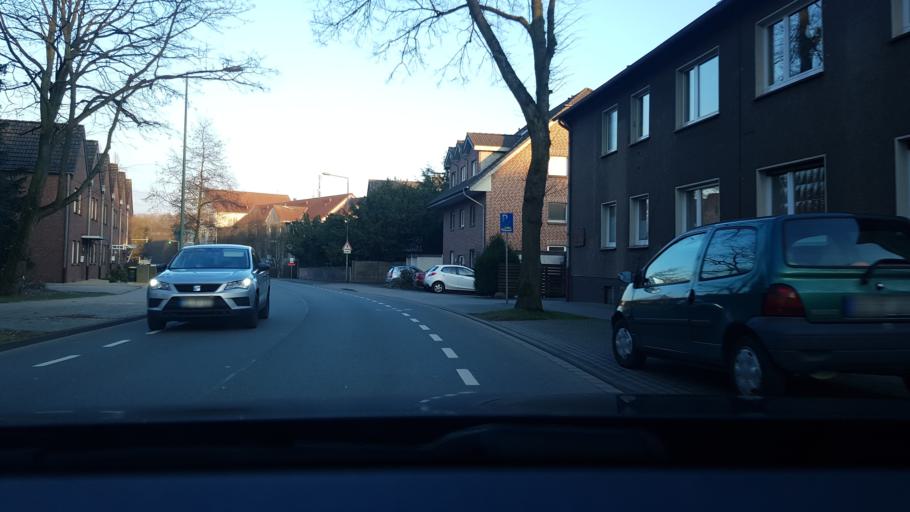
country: DE
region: North Rhine-Westphalia
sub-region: Regierungsbezirk Dusseldorf
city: Hochfeld
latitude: 51.4068
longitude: 6.7013
